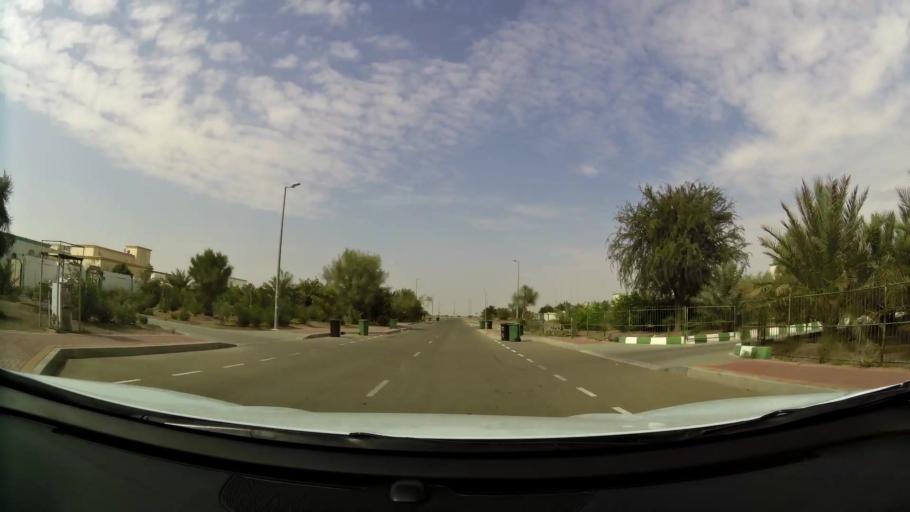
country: AE
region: Abu Dhabi
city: Al Ain
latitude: 24.1003
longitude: 55.8973
